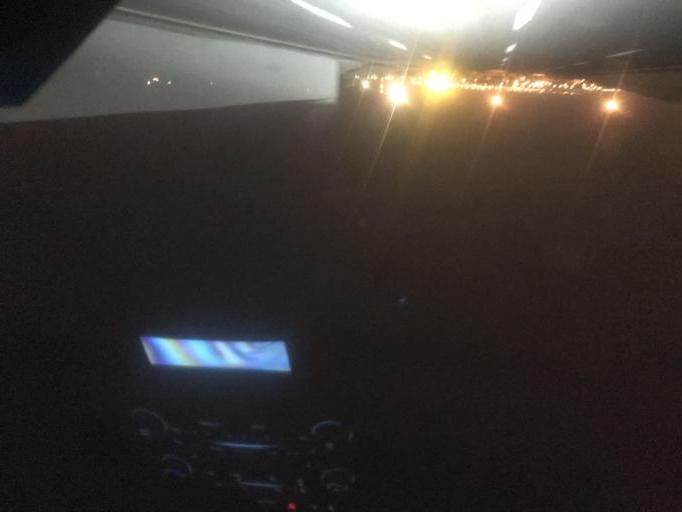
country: SA
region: Ar Riyad
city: Riyadh
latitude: 24.7617
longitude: 46.5865
